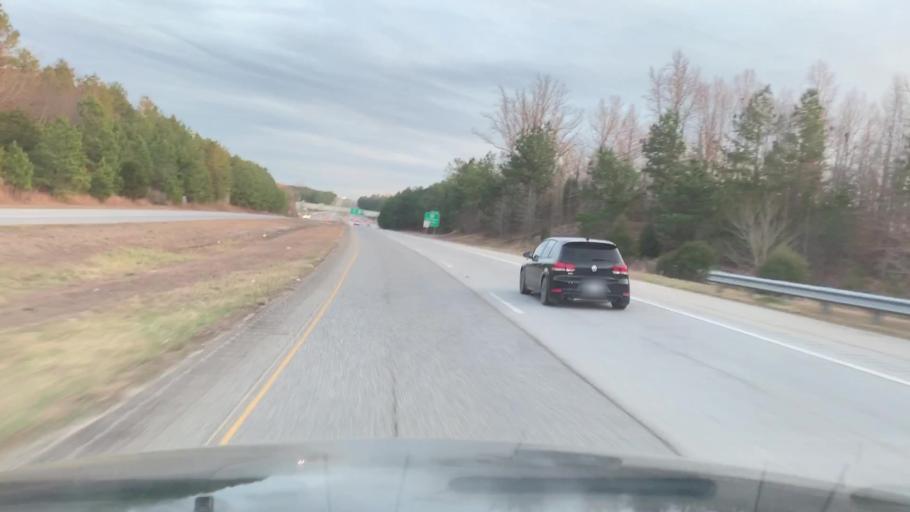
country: US
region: South Carolina
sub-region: Greenville County
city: Golden Grove
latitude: 34.7556
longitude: -82.4522
